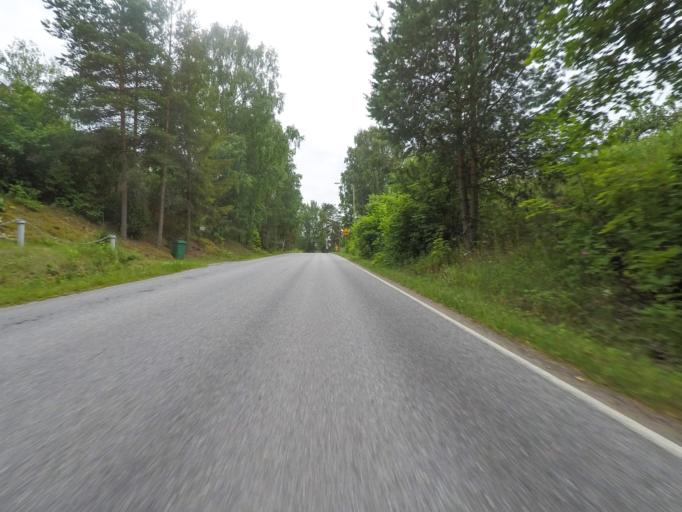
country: FI
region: Varsinais-Suomi
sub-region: Salo
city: Muurla
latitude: 60.3509
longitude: 23.2820
